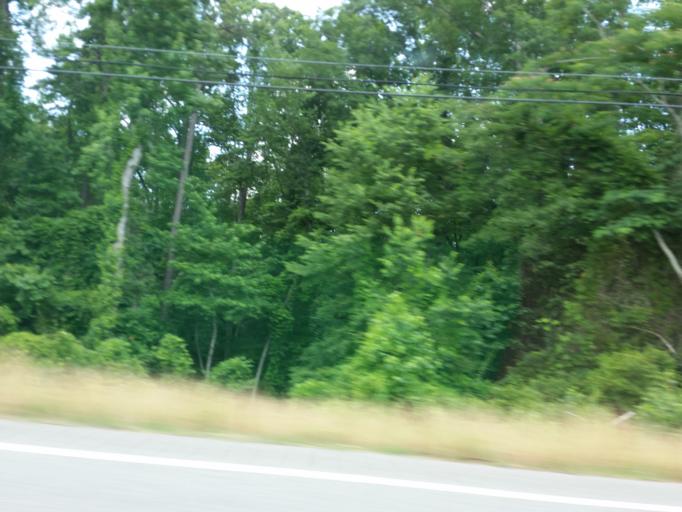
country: US
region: Alabama
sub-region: Sumter County
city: York
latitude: 32.4157
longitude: -88.2381
